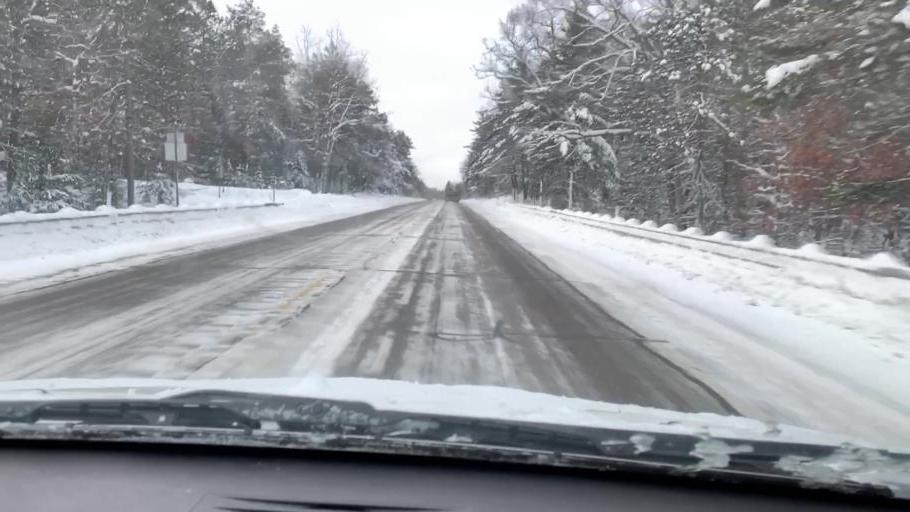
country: US
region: Michigan
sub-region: Wexford County
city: Manton
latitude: 44.5563
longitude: -85.3685
